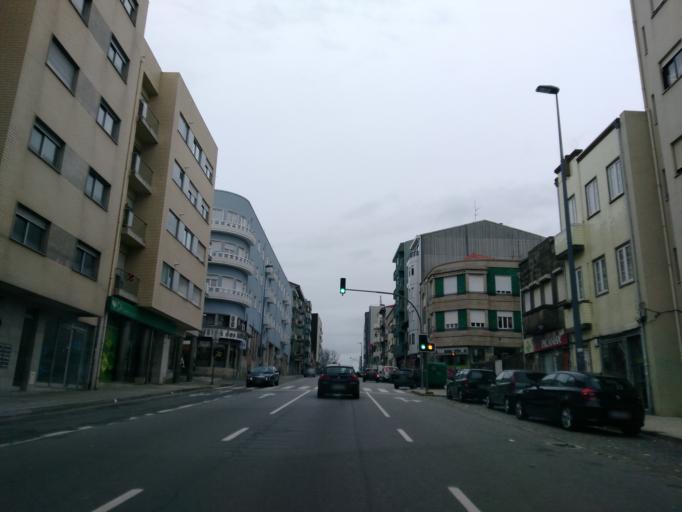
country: PT
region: Porto
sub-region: Porto
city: Porto
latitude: 41.1589
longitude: -8.5931
